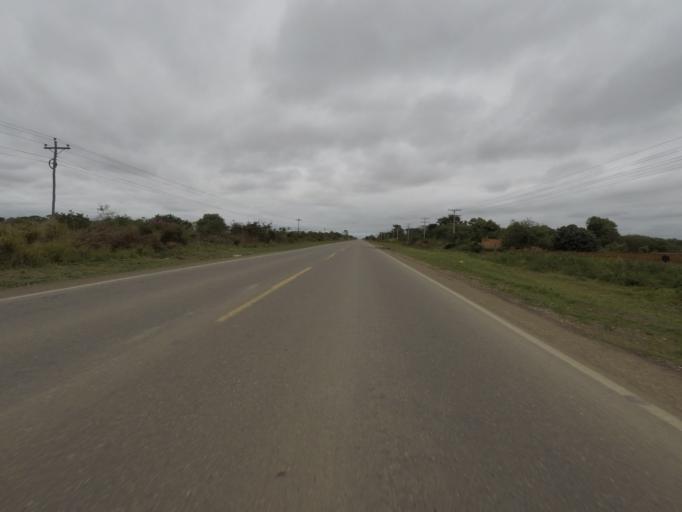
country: BO
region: Santa Cruz
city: Okinawa Numero Uno
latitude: -17.2290
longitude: -62.5555
